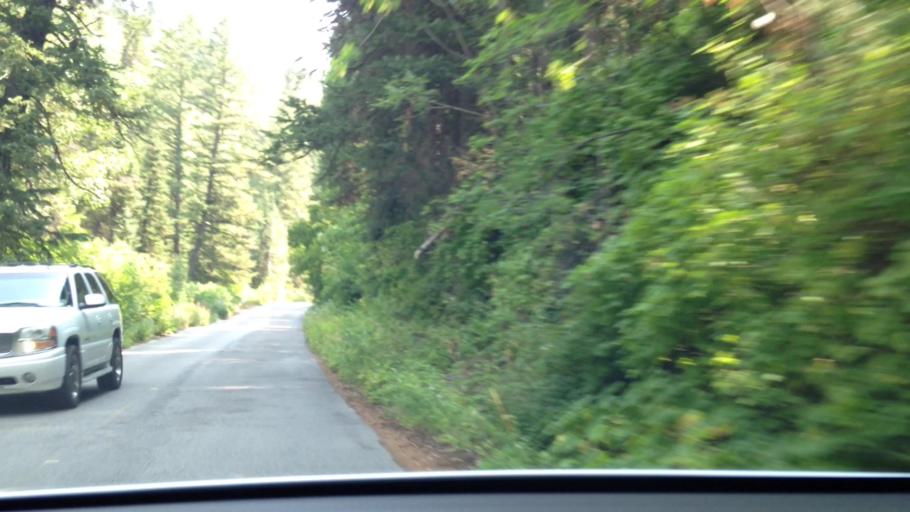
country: US
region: Utah
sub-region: Summit County
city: Summit Park
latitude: 40.6890
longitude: -111.6622
